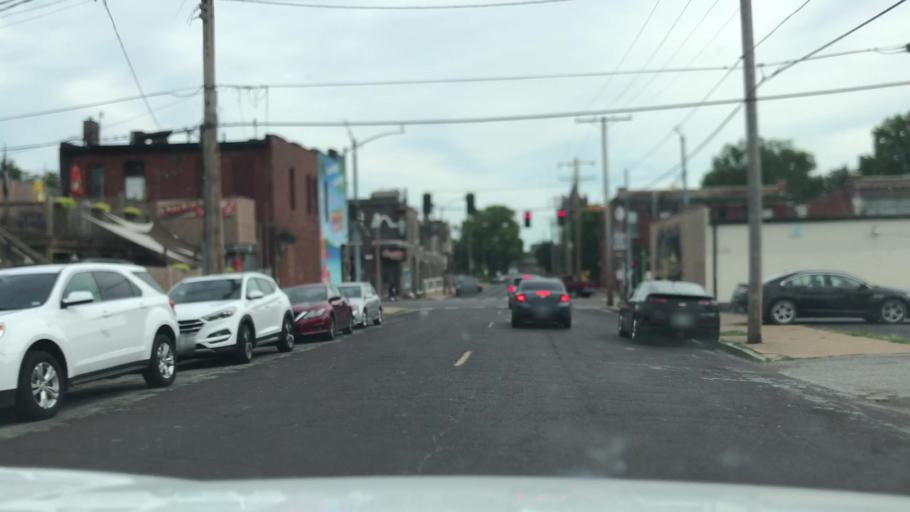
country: US
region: Missouri
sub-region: City of Saint Louis
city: St. Louis
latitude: 38.6279
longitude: -90.2543
